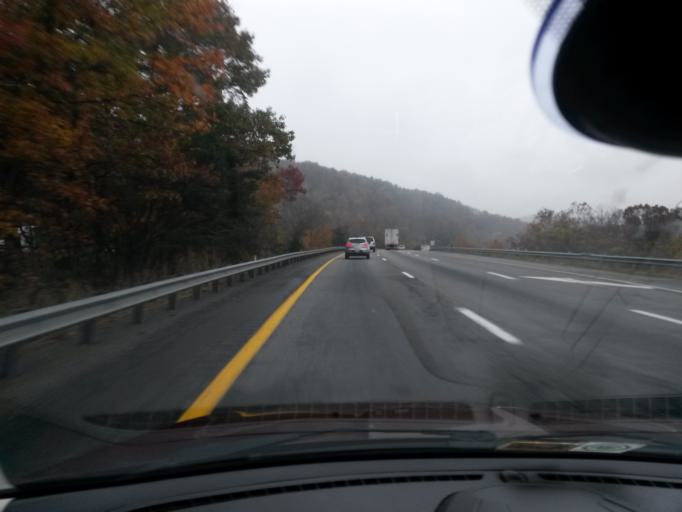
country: US
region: Virginia
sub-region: Montgomery County
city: Shawsville
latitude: 37.2359
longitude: -80.2350
